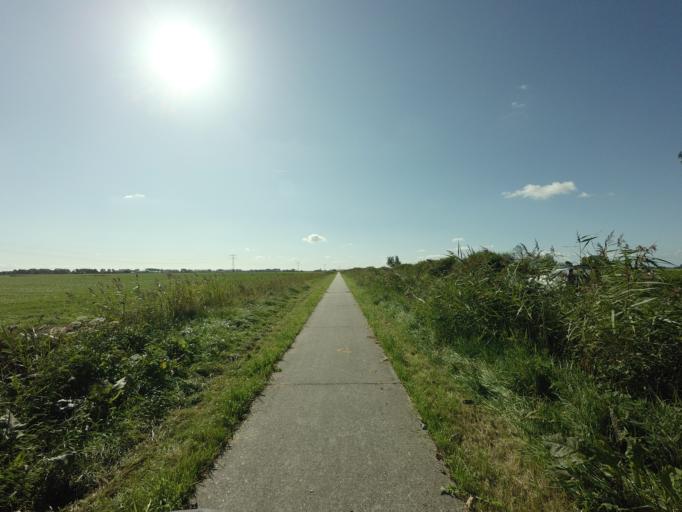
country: NL
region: Friesland
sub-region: Gemeente Boarnsterhim
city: Reduzum
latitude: 53.1479
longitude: 5.7636
